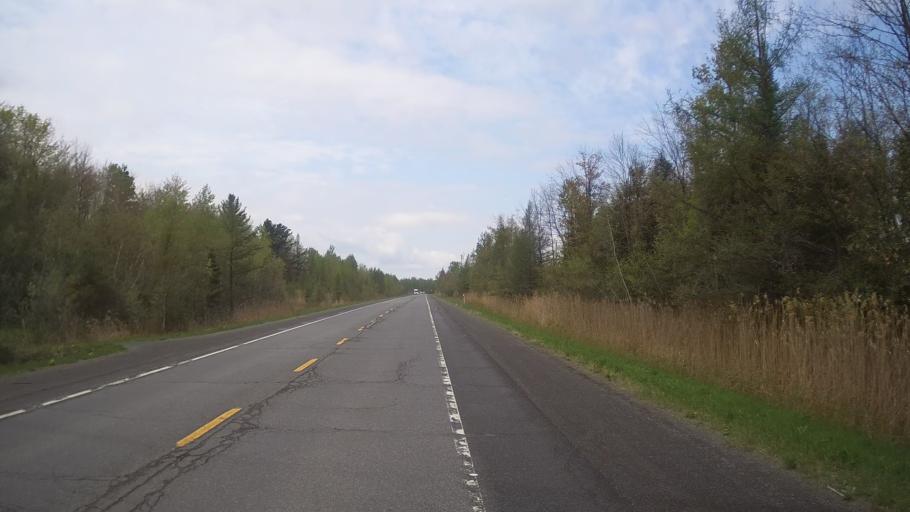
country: CA
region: Quebec
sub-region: Monteregie
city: Cowansville
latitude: 45.1953
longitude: -72.7333
